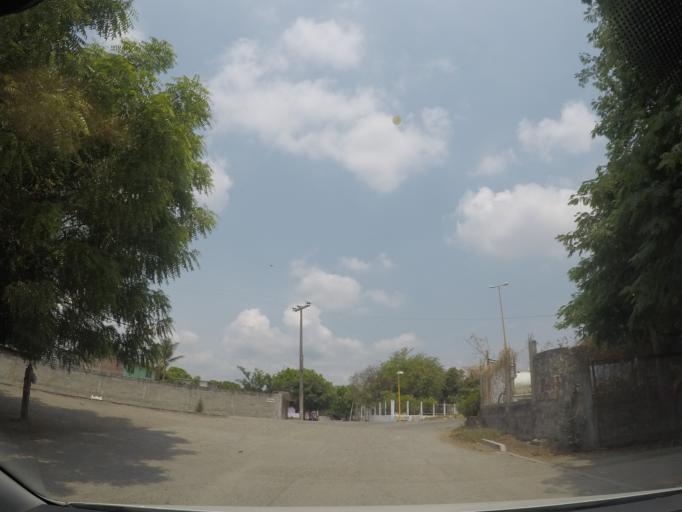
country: MX
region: Oaxaca
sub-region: El Espinal
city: El Espinal
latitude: 16.4919
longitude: -95.0442
